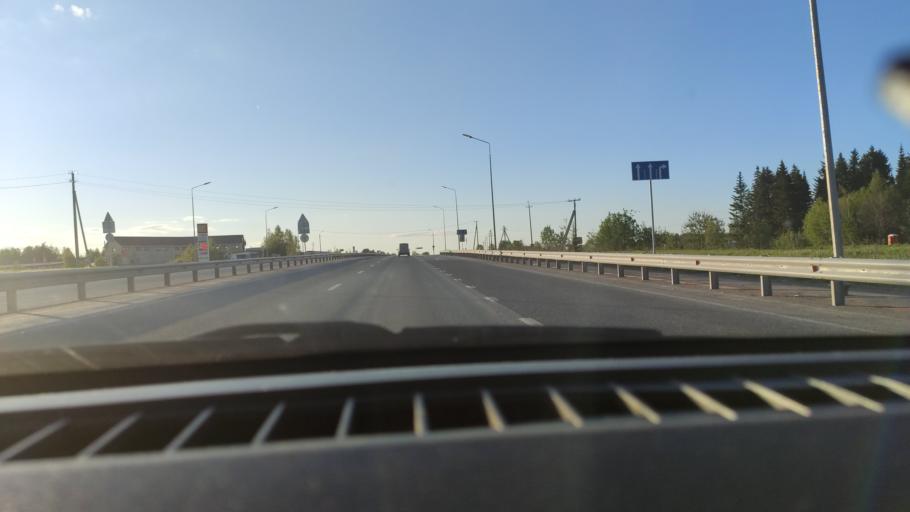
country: RU
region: Perm
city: Polazna
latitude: 58.2022
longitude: 56.4019
